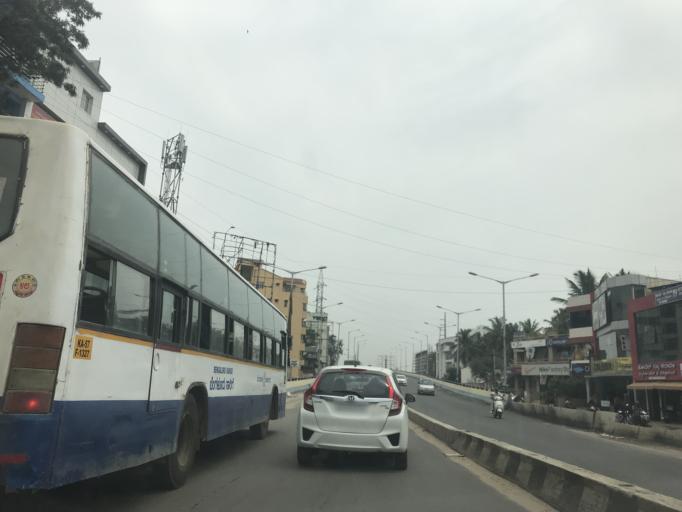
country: IN
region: Karnataka
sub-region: Bangalore Urban
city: Bangalore
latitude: 13.0303
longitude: 77.6349
